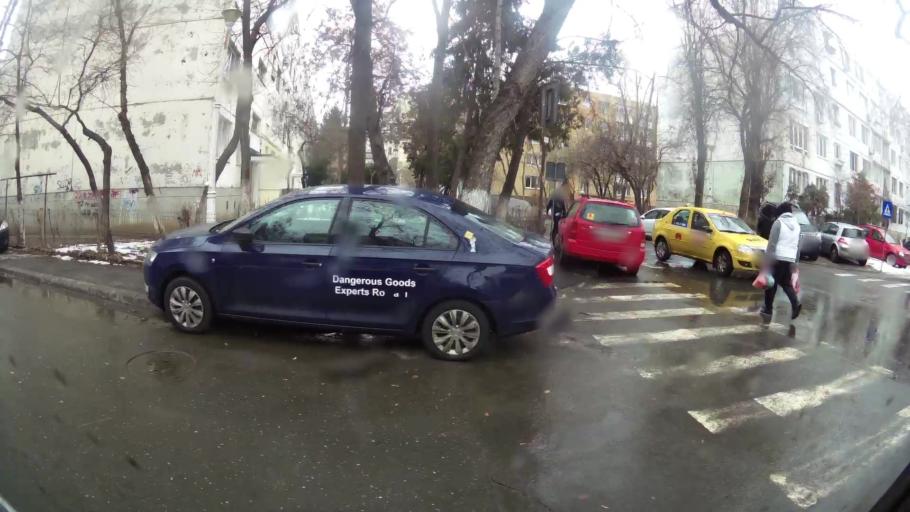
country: RO
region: Ilfov
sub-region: Comuna Chiajna
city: Rosu
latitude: 44.4235
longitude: 26.0178
